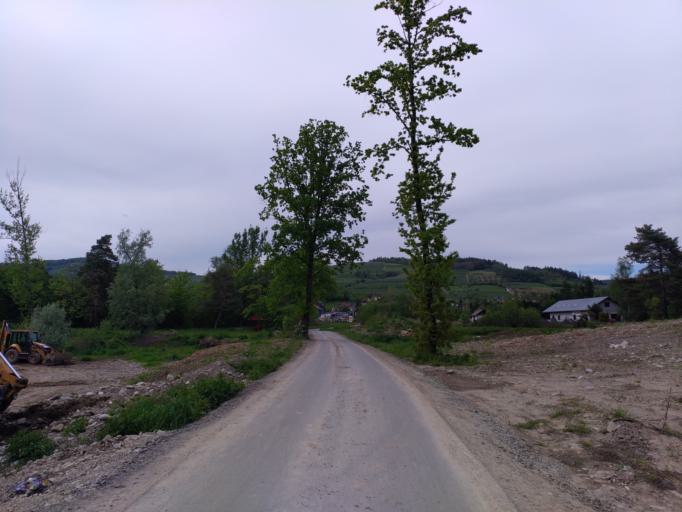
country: PL
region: Lesser Poland Voivodeship
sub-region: Powiat nowosadecki
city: Lacko
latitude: 49.5507
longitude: 20.4307
